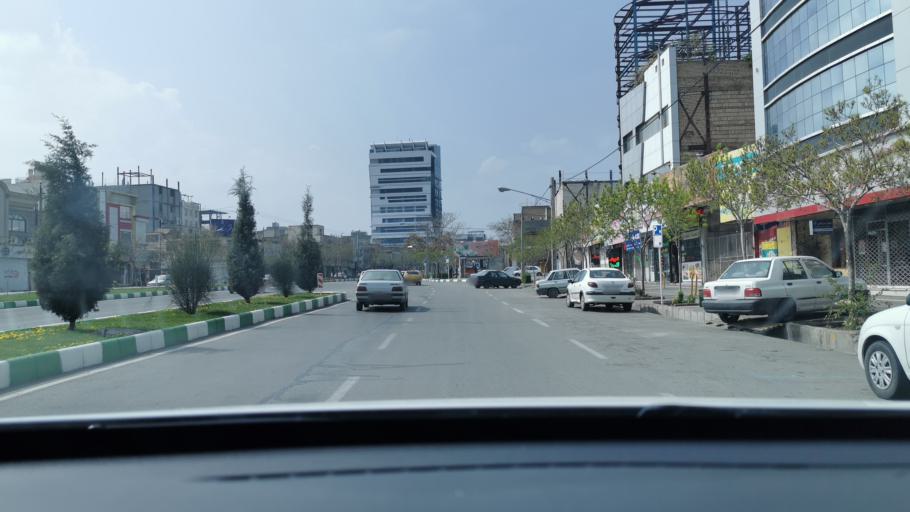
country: IR
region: Razavi Khorasan
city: Mashhad
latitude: 36.3294
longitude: 59.5263
